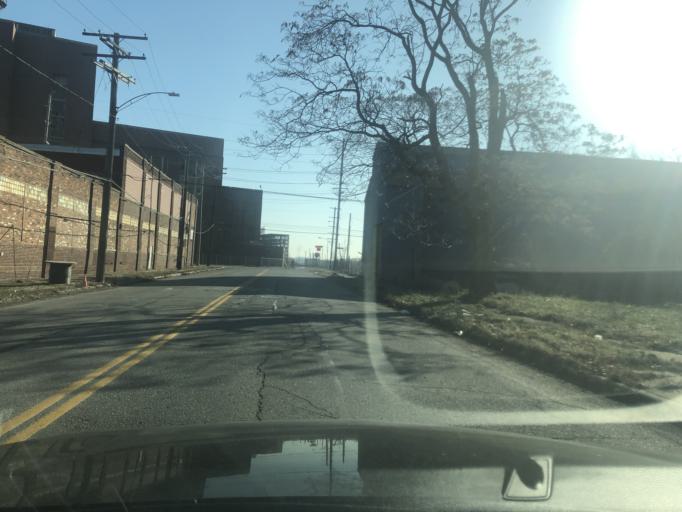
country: US
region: Michigan
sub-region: Wayne County
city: River Rouge
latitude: 42.3045
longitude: -83.0923
